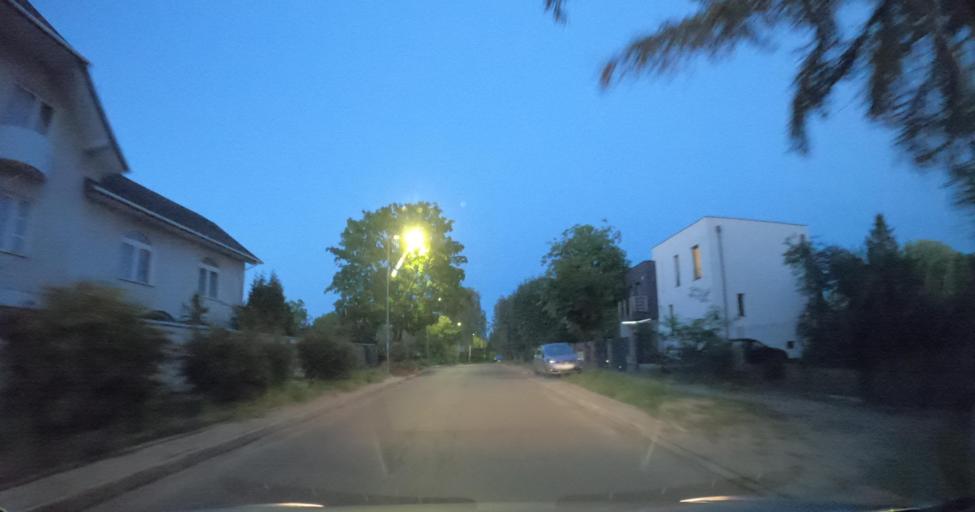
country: PL
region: Pomeranian Voivodeship
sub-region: Gdynia
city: Wielki Kack
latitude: 54.4268
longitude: 18.4659
